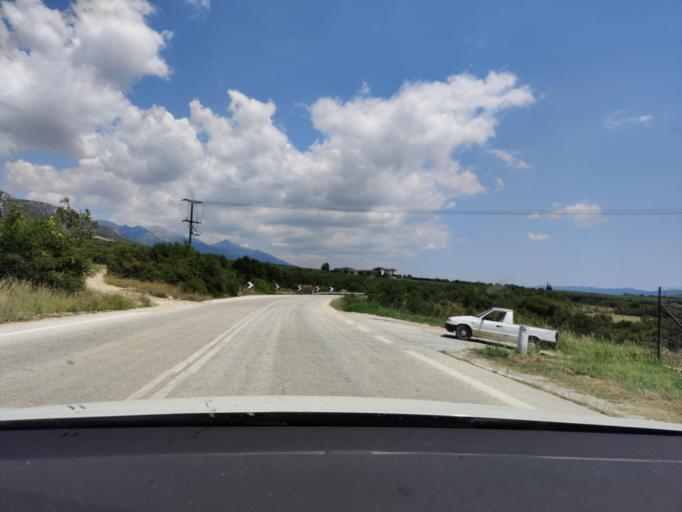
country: GR
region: East Macedonia and Thrace
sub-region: Nomos Kavalas
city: Paralia Ofryniou
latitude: 40.8090
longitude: 23.9834
